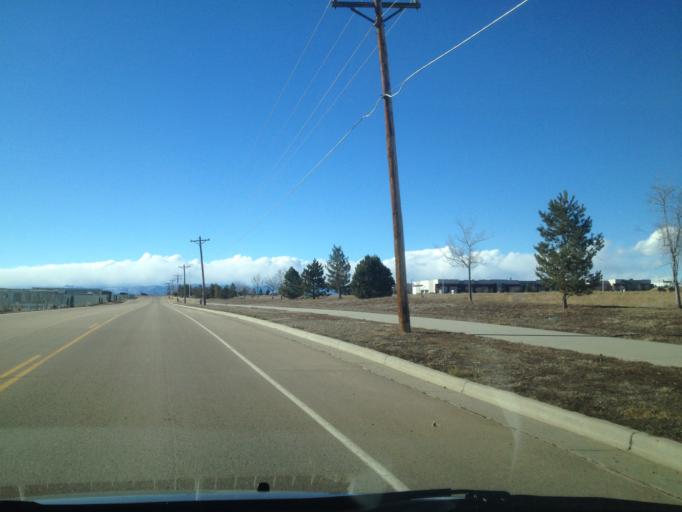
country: US
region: Colorado
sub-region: Weld County
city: Dacono
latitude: 40.0731
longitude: -104.9747
